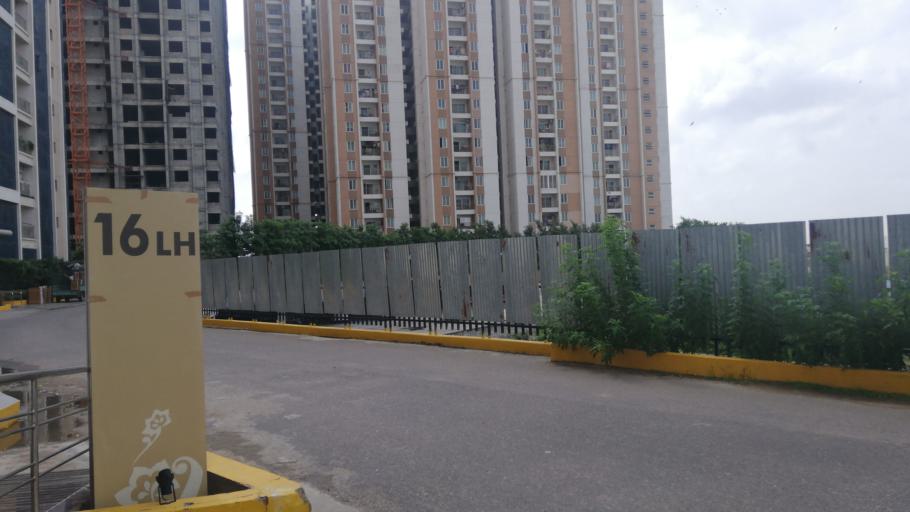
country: IN
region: Telangana
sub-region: Hyderabad
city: Hyderabad
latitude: 17.4094
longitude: 78.3757
